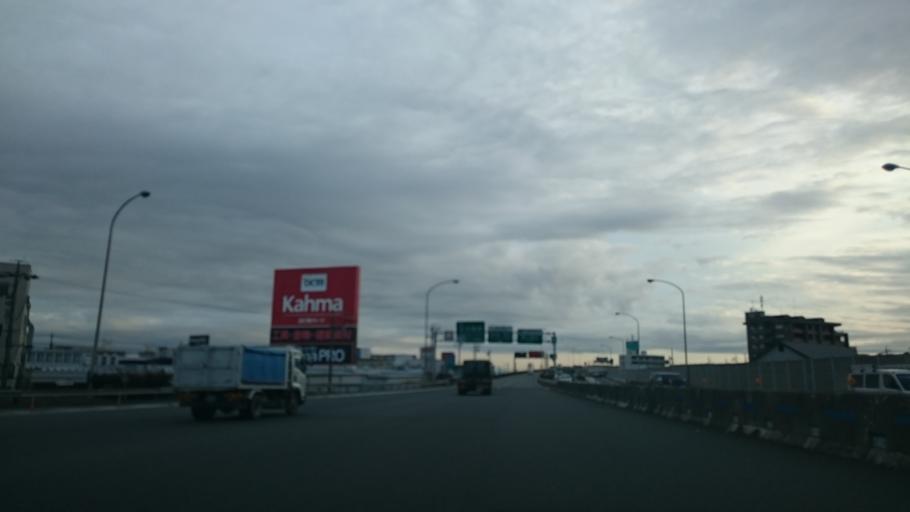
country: JP
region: Aichi
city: Kanie
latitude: 35.1540
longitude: 136.8063
